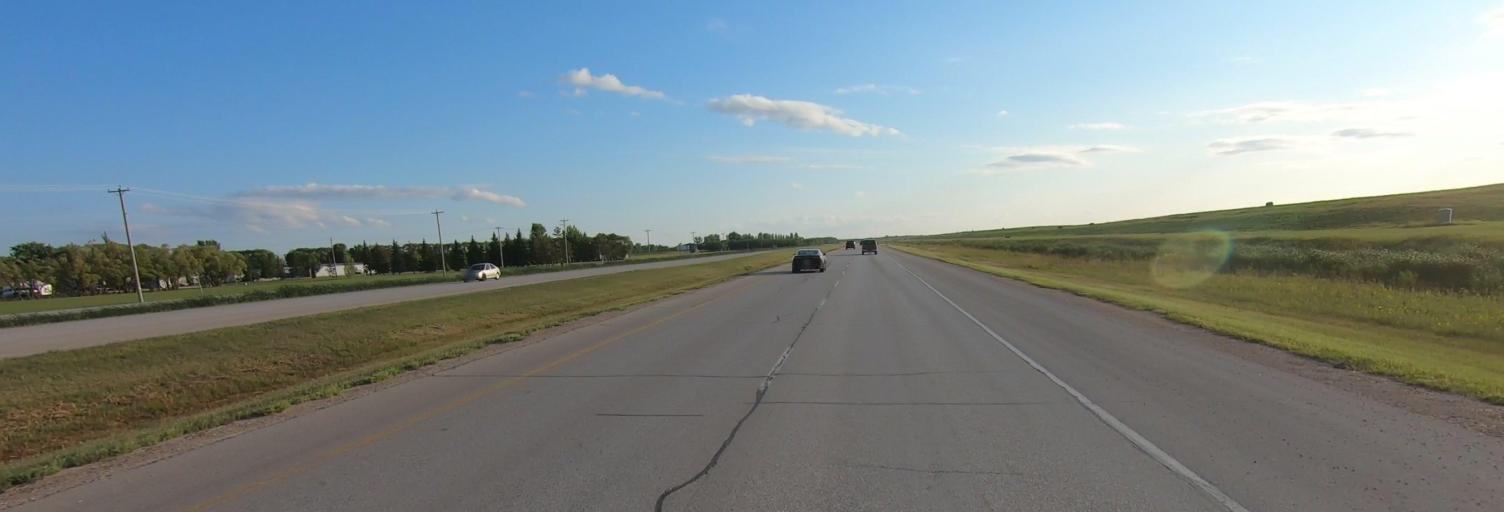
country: CA
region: Manitoba
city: Selkirk
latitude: 50.0094
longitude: -96.9552
